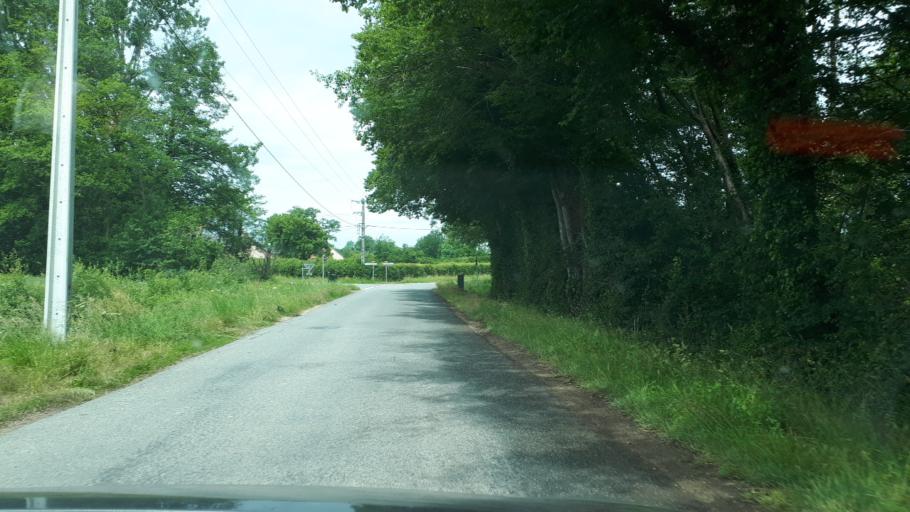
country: FR
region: Centre
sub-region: Departement du Cher
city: Henrichemont
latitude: 47.3974
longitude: 2.6533
